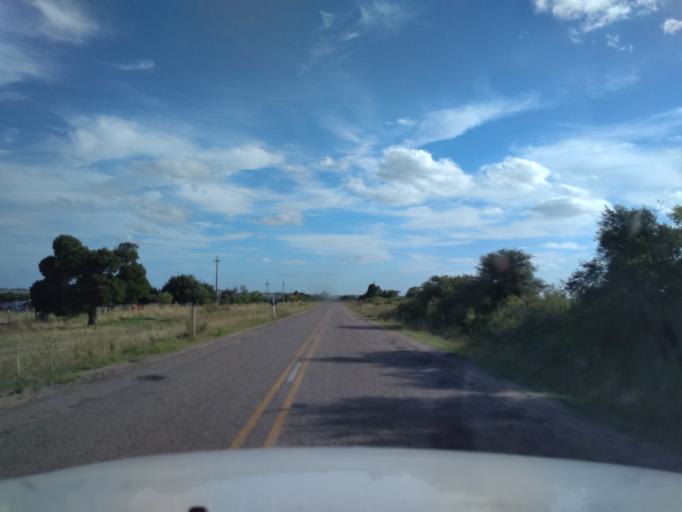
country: UY
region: Canelones
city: San Ramon
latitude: -34.2608
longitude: -55.9272
